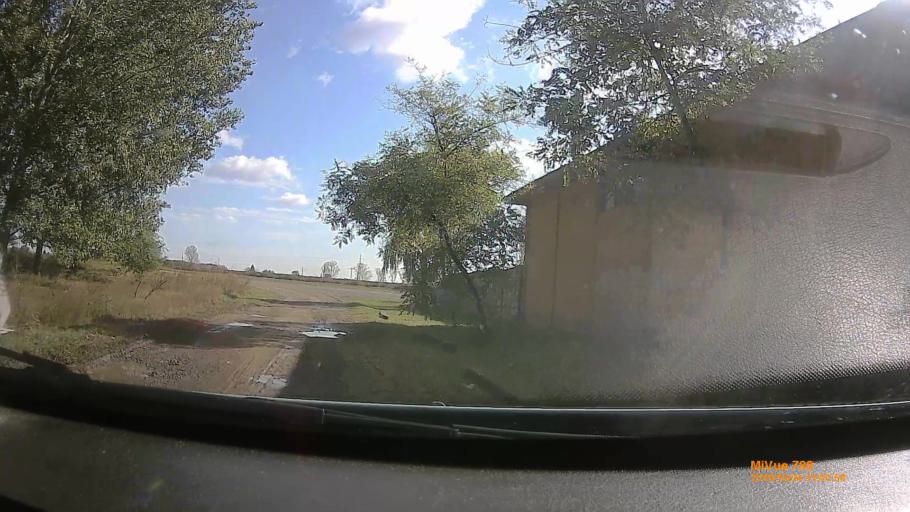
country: HU
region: Szabolcs-Szatmar-Bereg
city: Nyirtelek
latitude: 47.9821
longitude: 21.6714
